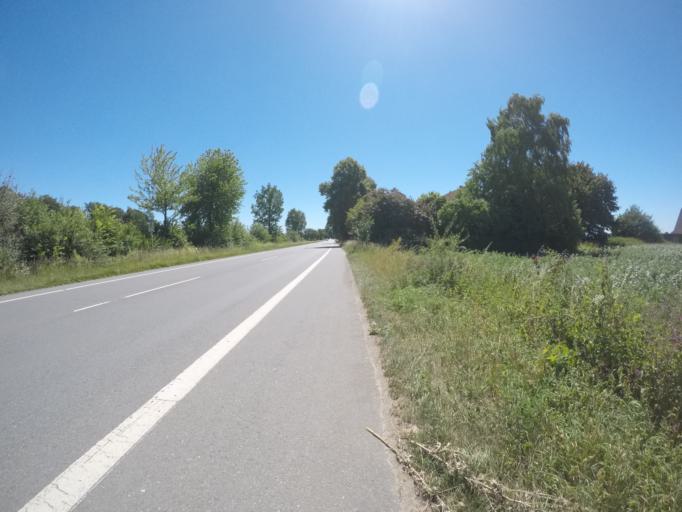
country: DE
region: North Rhine-Westphalia
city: Enger
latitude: 52.0848
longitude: 8.5850
